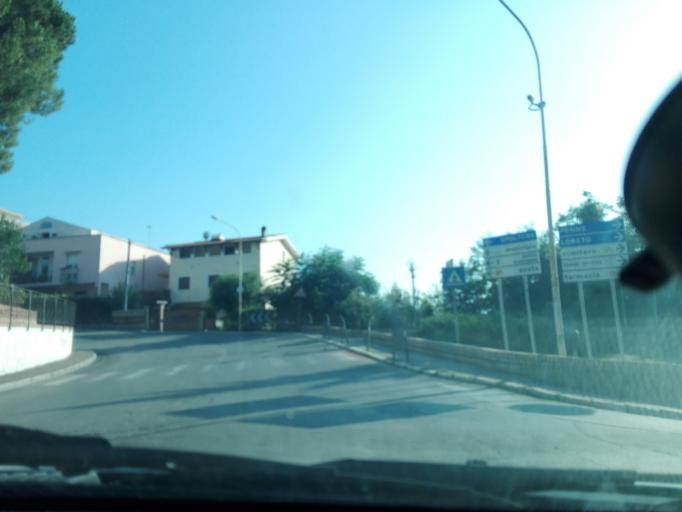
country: IT
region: Abruzzo
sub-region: Provincia di Pescara
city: Cappelle sul Tavo
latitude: 42.4647
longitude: 14.1033
